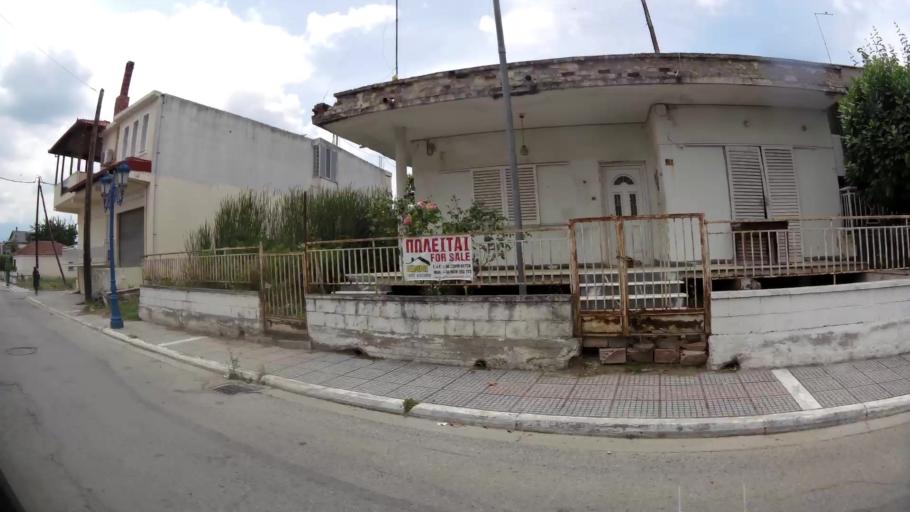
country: GR
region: Central Macedonia
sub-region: Nomos Pierias
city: Kallithea
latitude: 40.2748
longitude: 22.5764
